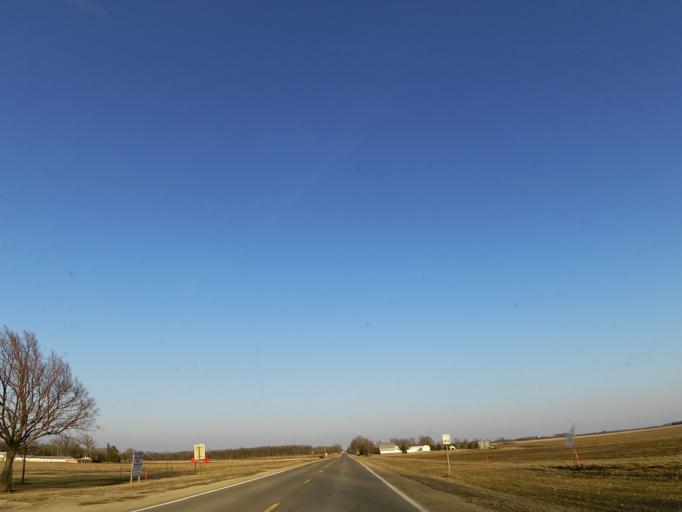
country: US
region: Iowa
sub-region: Mitchell County
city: Saint Ansgar
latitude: 43.4150
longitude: -93.0138
